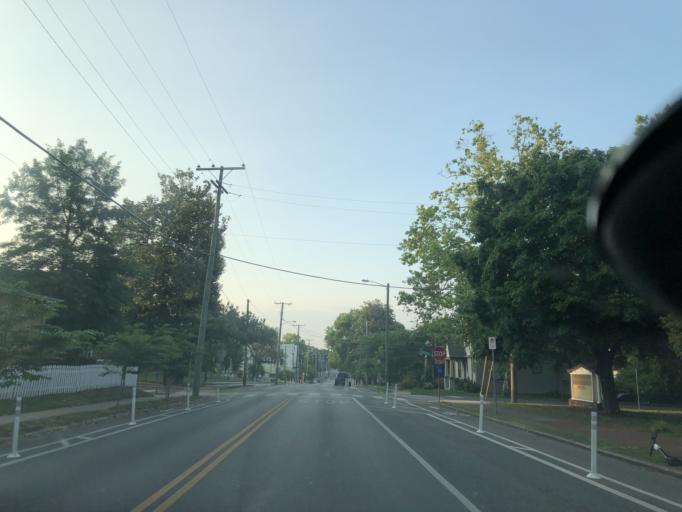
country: US
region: Tennessee
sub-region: Davidson County
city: Oak Hill
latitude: 36.1252
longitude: -86.7863
